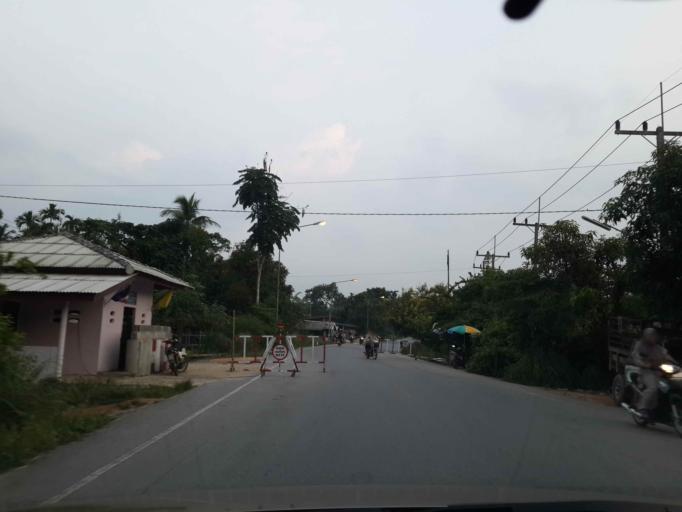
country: TH
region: Narathiwat
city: Rueso
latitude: 6.3611
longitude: 101.4677
